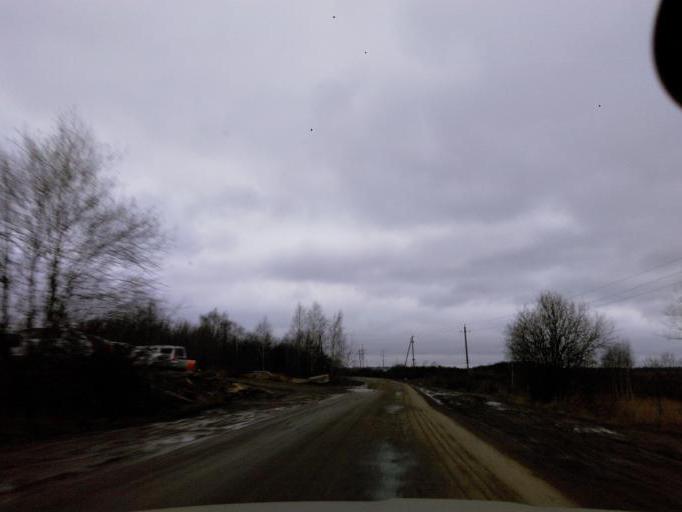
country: RU
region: Moskovskaya
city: Radumlya
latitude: 56.0577
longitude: 37.1344
